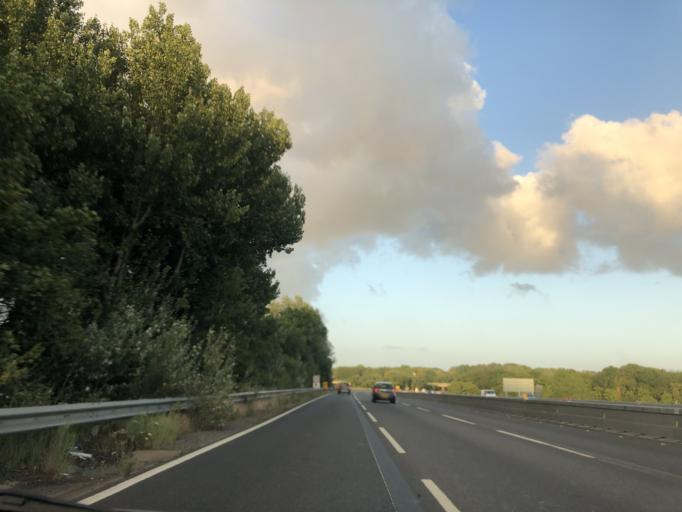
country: GB
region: England
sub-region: Hampshire
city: Bursledon
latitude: 50.8896
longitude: -1.2985
